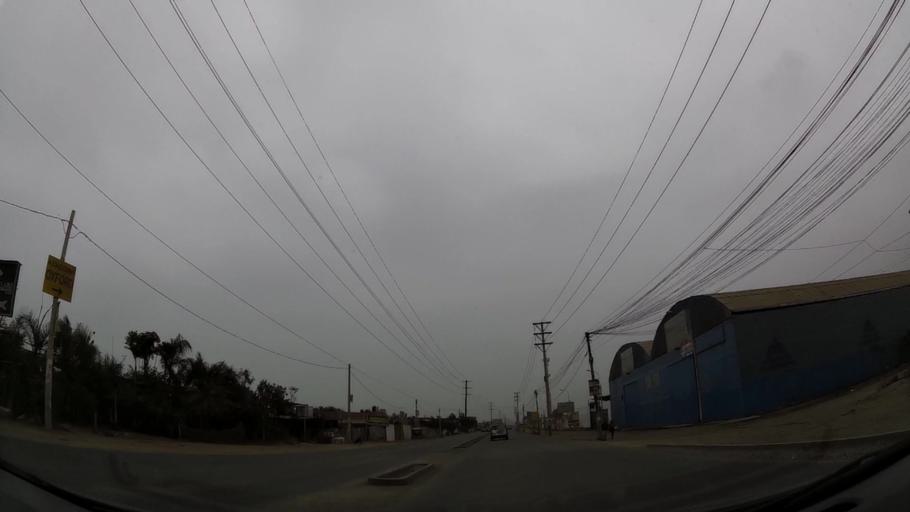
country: PE
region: Lima
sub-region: Lima
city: Punta Hermosa
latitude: -12.2836
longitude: -76.8638
